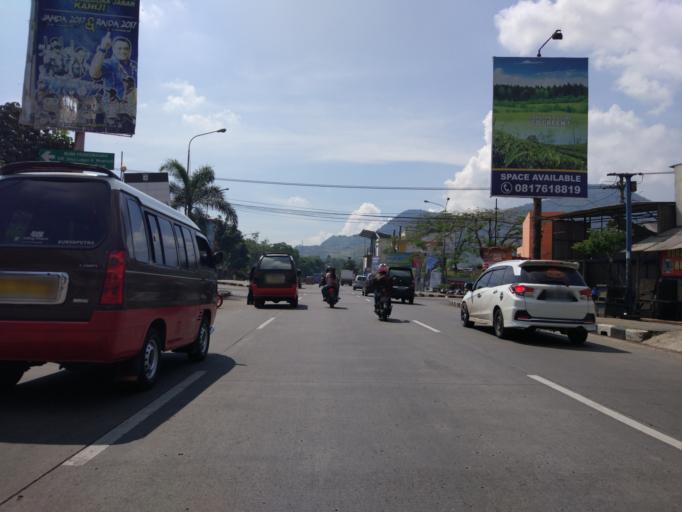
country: ID
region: West Java
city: Cileunyi
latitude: -6.9332
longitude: 107.7714
